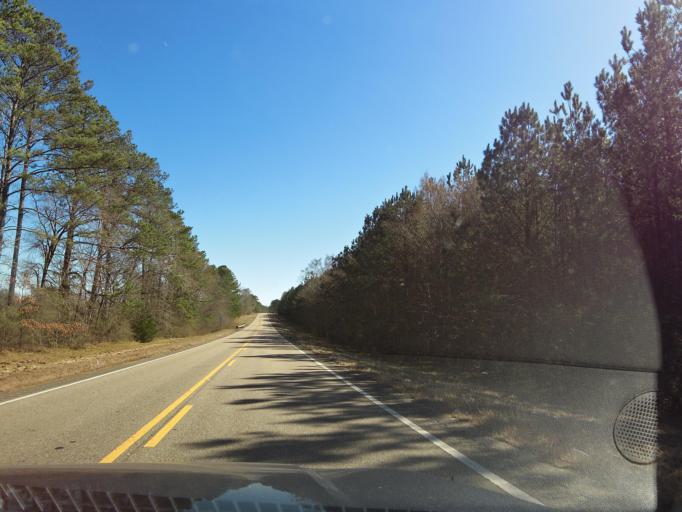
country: US
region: Alabama
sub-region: Montgomery County
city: Pike Road
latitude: 32.1706
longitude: -86.0728
